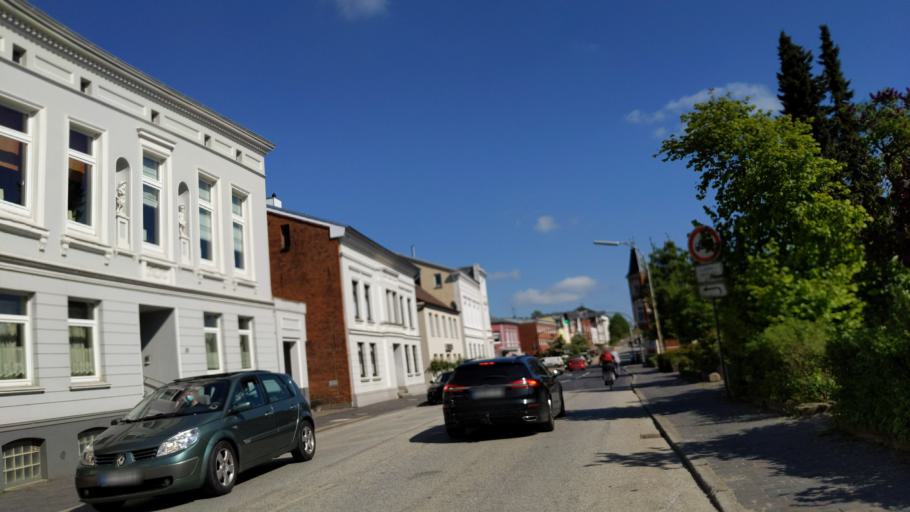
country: DE
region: Schleswig-Holstein
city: Eutin
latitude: 54.1332
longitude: 10.6114
